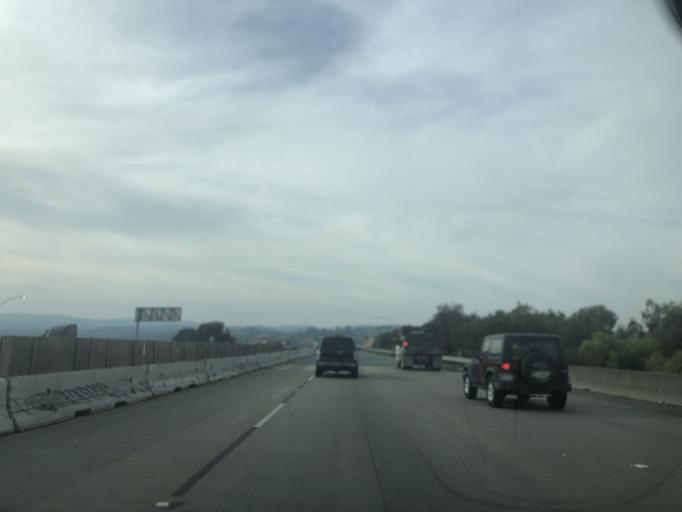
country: US
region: California
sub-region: Contra Costa County
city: Pacheco
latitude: 38.0012
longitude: -122.0530
